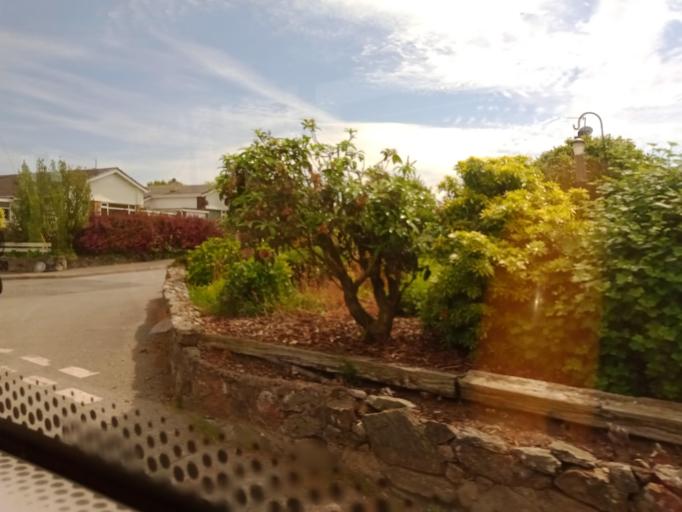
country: GB
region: Wales
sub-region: Gwynedd
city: Bangor
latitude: 53.2509
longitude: -4.1441
